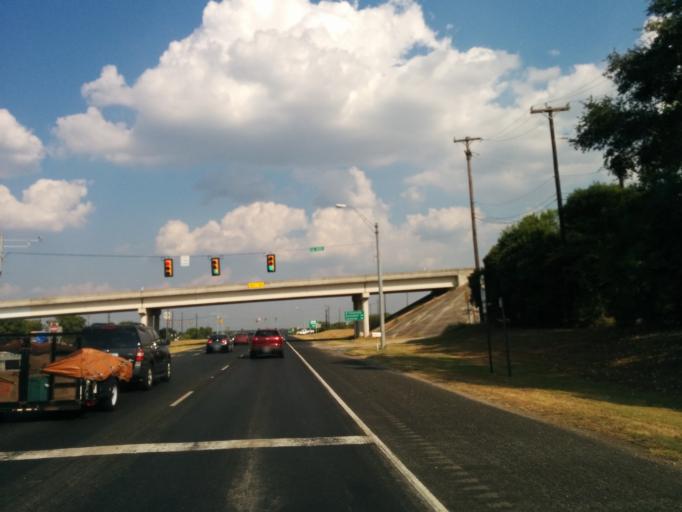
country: US
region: Texas
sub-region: Bexar County
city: Elmendorf
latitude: 29.2676
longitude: -98.3072
